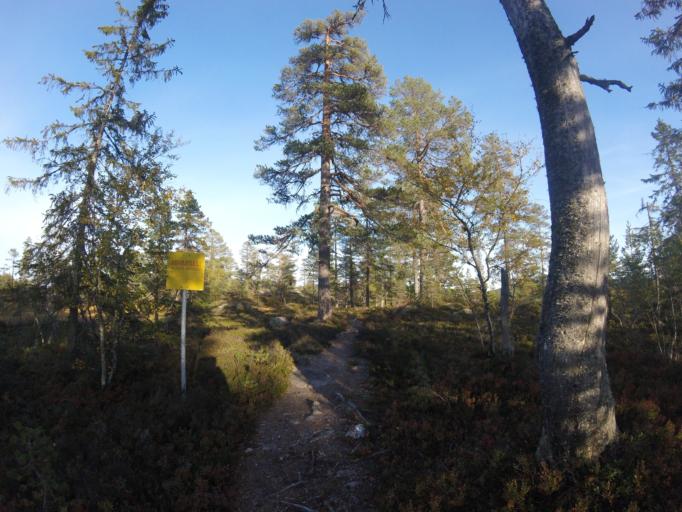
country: NO
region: Telemark
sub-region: Notodden
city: Notodden
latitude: 59.6790
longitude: 9.4180
